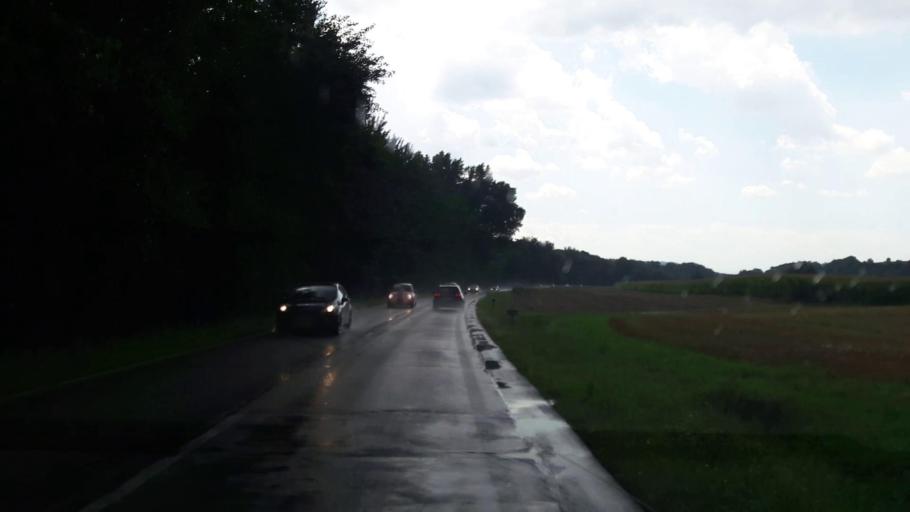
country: AT
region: Lower Austria
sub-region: Politischer Bezirk Krems
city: Aggsbach
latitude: 48.2696
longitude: 15.3753
